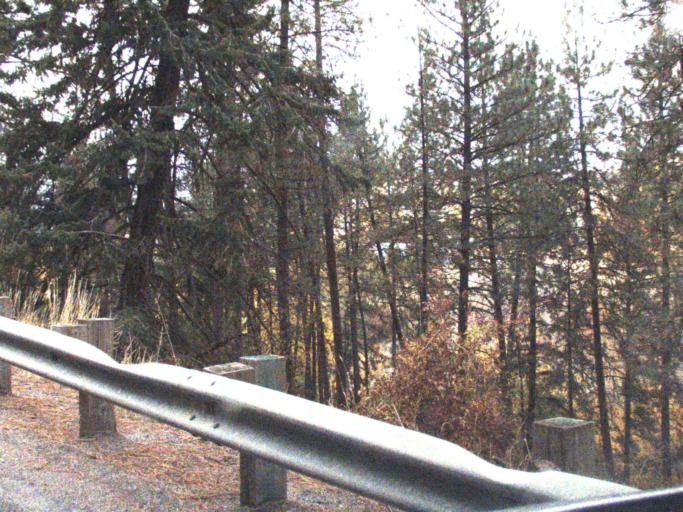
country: US
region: Washington
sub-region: Lincoln County
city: Davenport
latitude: 48.1170
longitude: -118.1968
